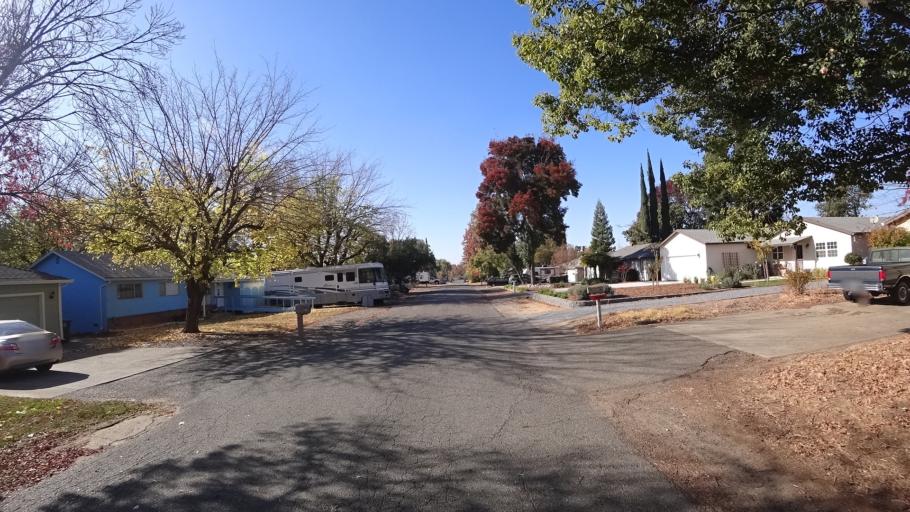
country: US
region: California
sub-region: Sacramento County
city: Citrus Heights
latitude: 38.7045
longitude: -121.2770
